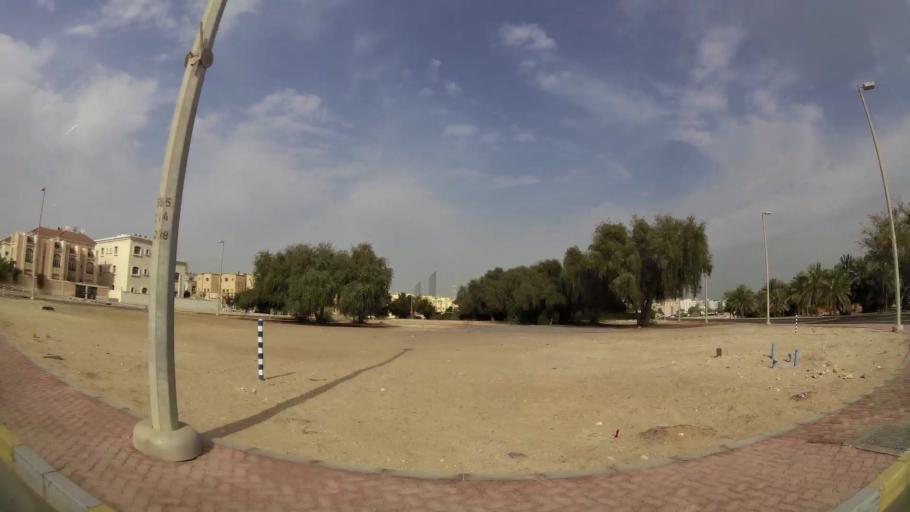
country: AE
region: Abu Dhabi
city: Abu Dhabi
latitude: 24.4736
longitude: 54.3900
